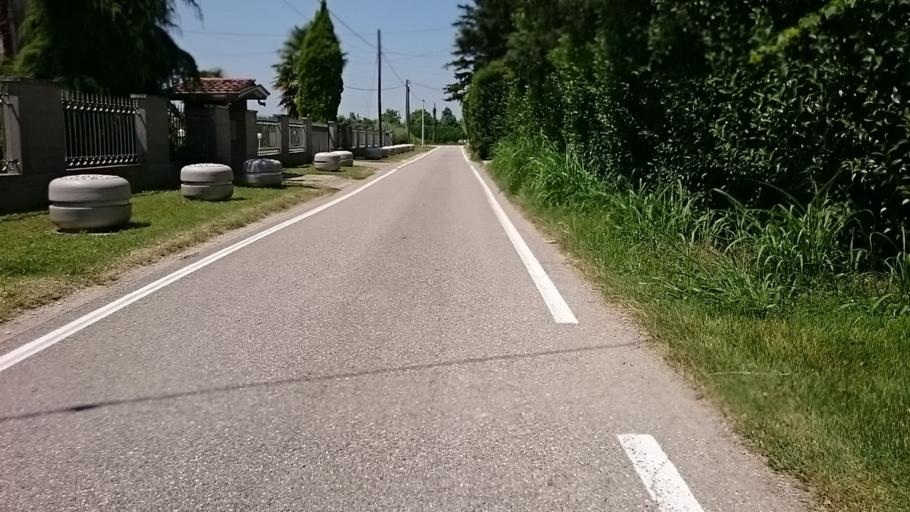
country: IT
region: Veneto
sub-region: Provincia di Padova
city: Villanova
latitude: 45.5102
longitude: 11.9867
